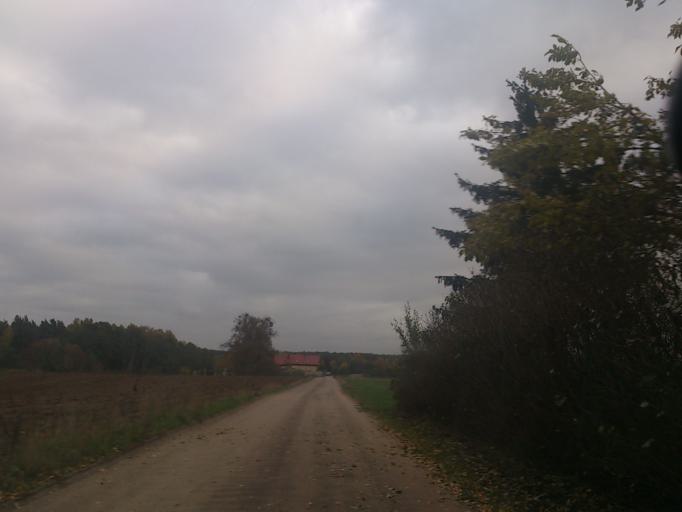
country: PL
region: Kujawsko-Pomorskie
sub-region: Powiat golubsko-dobrzynski
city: Golub-Dobrzyn
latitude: 53.1266
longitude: 19.0964
